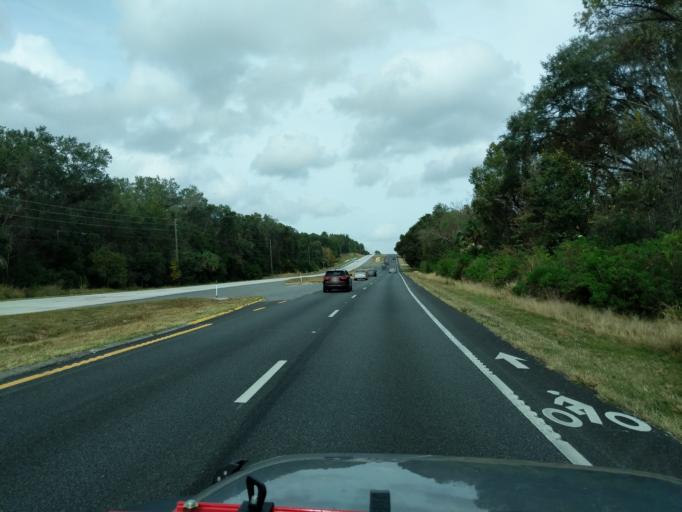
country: US
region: Florida
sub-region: Orange County
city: Tangerine
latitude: 28.7566
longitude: -81.6244
